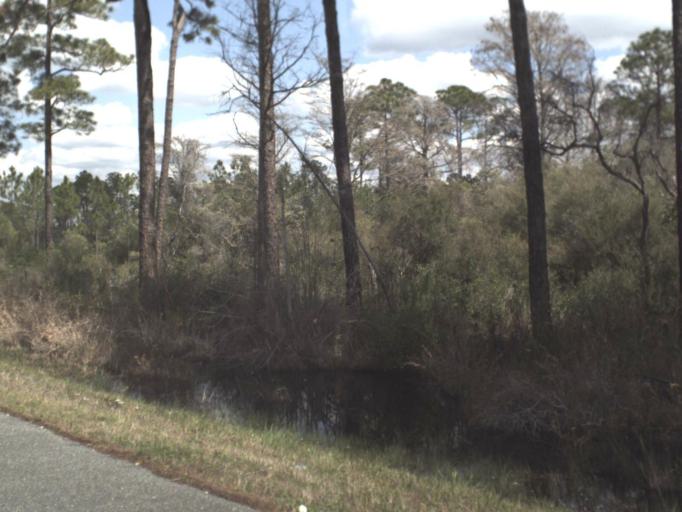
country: US
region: Florida
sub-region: Franklin County
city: Eastpoint
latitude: 29.7949
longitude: -84.8306
